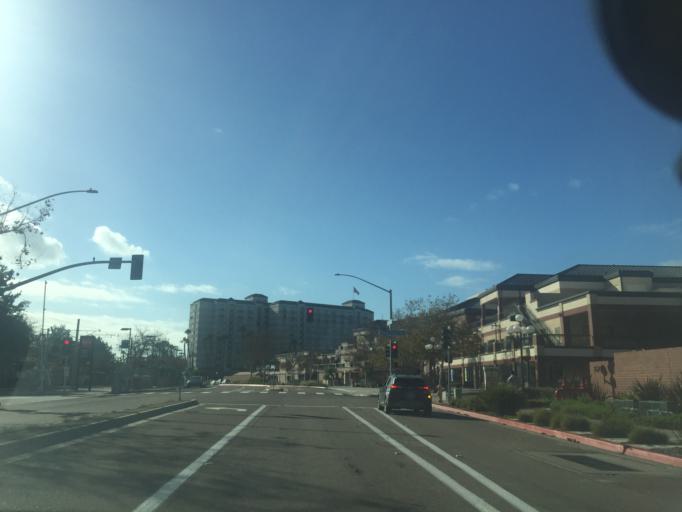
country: US
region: California
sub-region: San Diego County
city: San Diego
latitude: 32.7708
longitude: -117.1573
